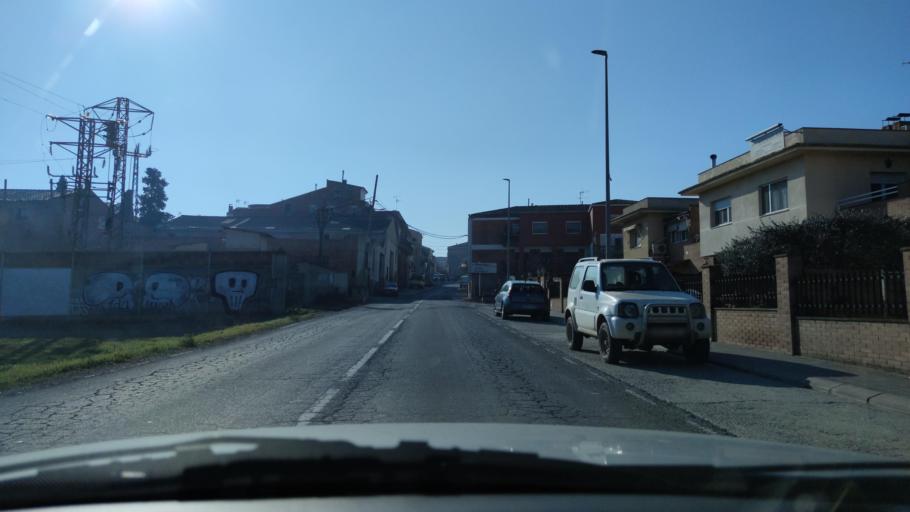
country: ES
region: Catalonia
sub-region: Provincia de Lleida
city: Aspa
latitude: 41.5458
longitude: 0.7348
